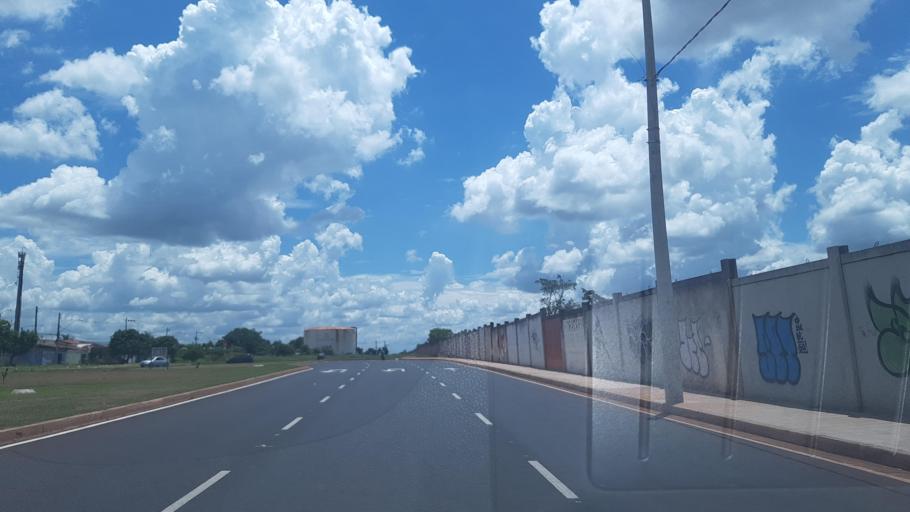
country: BR
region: Minas Gerais
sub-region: Uberlandia
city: Uberlandia
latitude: -18.9569
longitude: -48.3328
